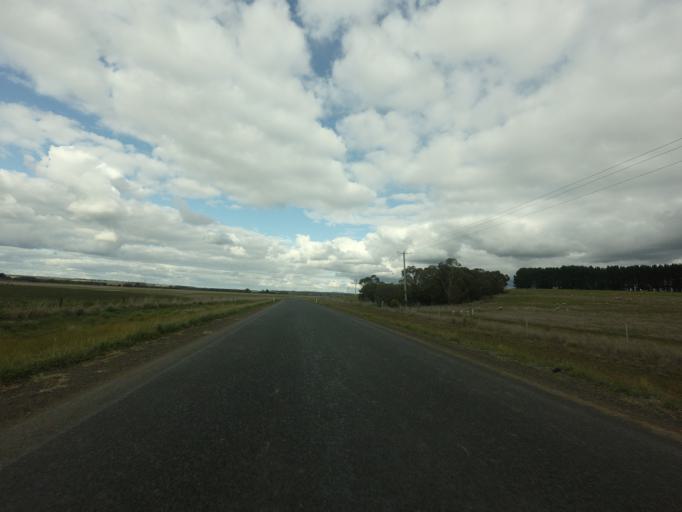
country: AU
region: Tasmania
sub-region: Northern Midlands
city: Longford
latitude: -41.7754
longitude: 147.0930
